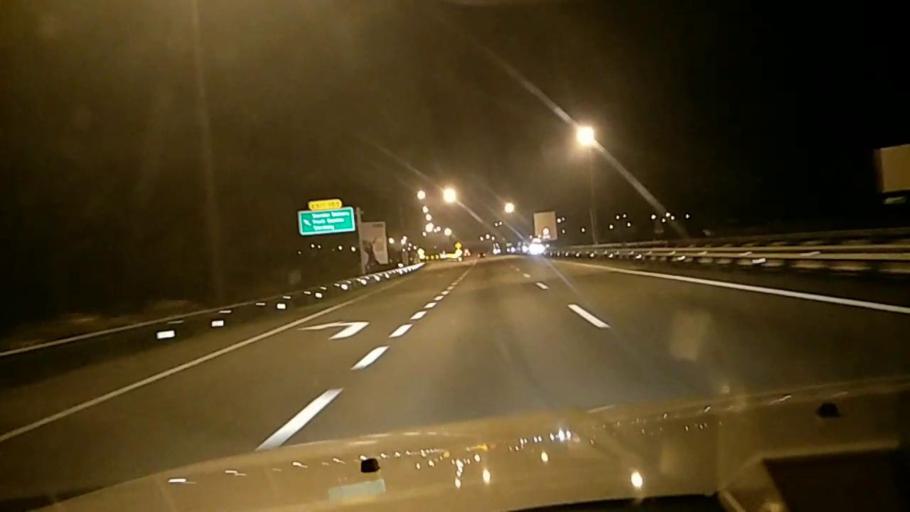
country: MY
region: Perak
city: Parit Buntar
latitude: 5.1053
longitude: 100.5612
